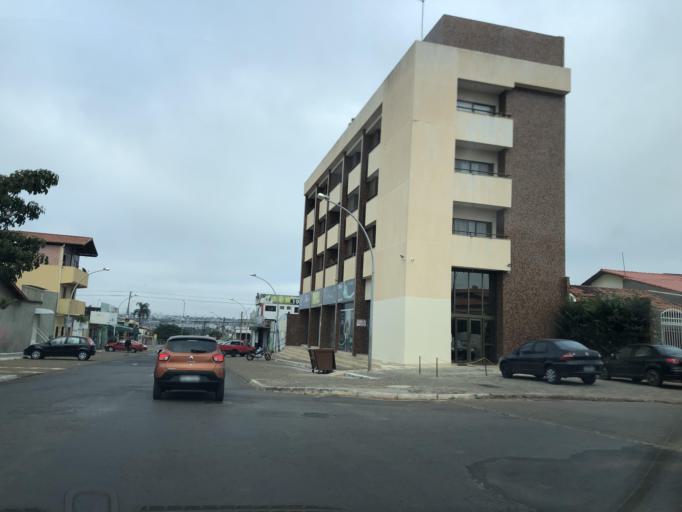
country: BR
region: Federal District
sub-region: Brasilia
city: Brasilia
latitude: -15.8162
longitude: -48.0655
